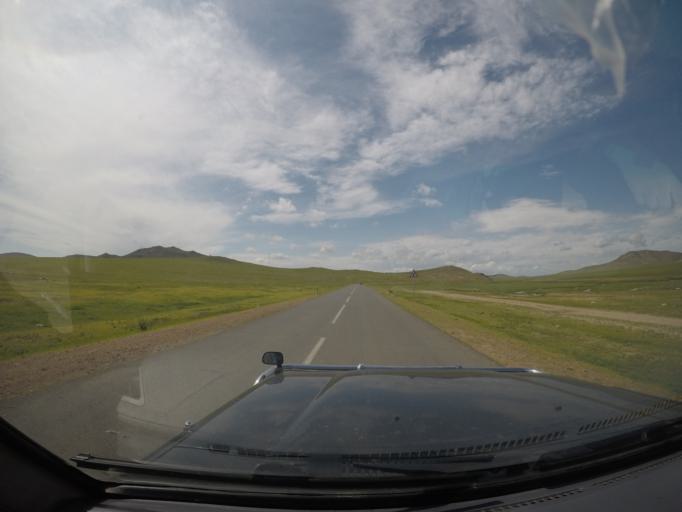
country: MN
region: Hentiy
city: Moron
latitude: 47.3914
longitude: 110.3004
